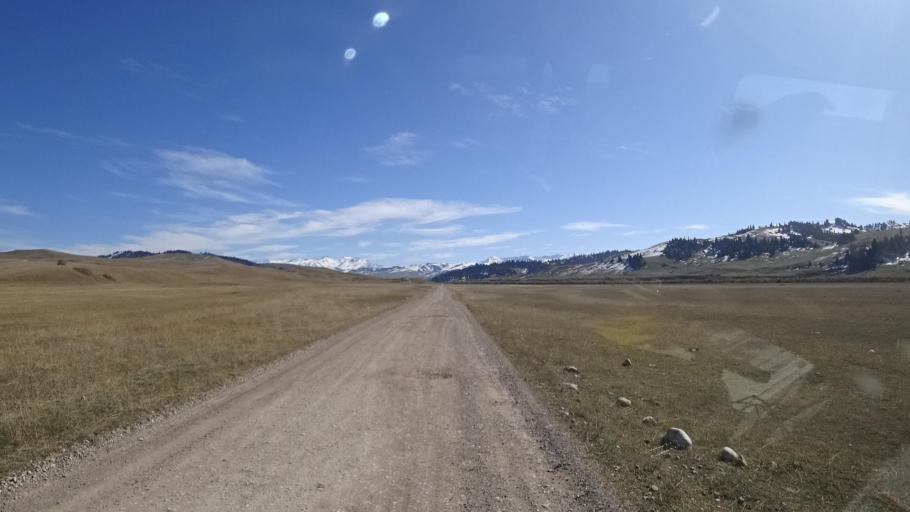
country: KZ
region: Almaty Oblysy
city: Kegen
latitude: 42.7448
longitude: 78.9955
